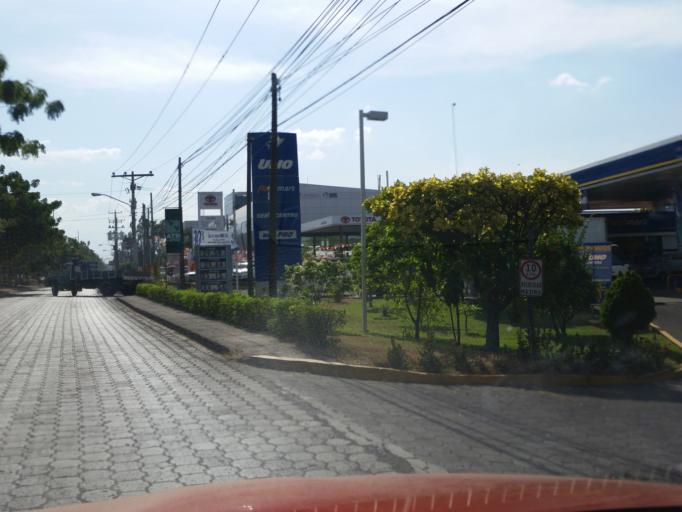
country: NI
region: Managua
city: Managua
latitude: 12.1127
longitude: -86.2605
